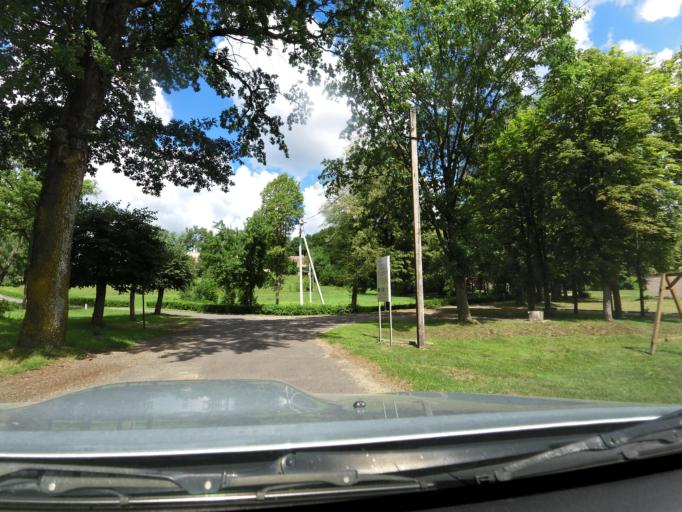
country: LT
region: Vilnius County
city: Elektrenai
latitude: 54.9536
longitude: 24.6553
